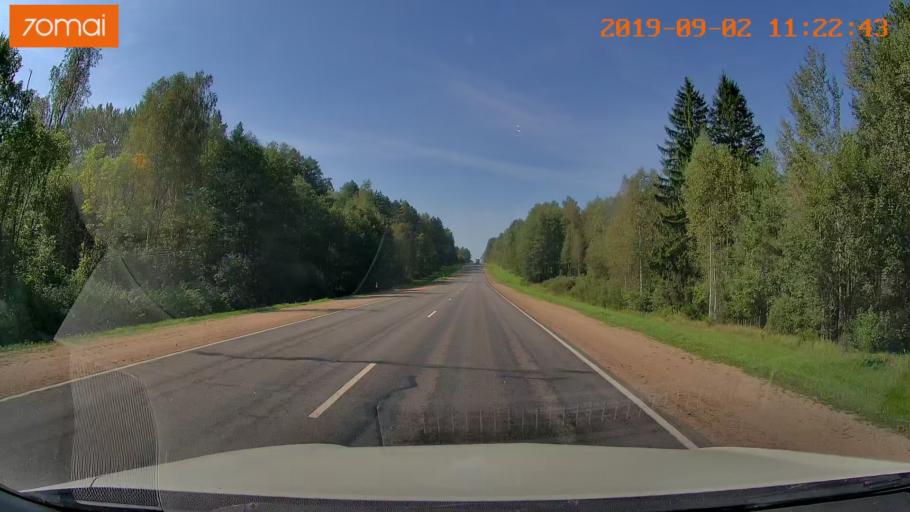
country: RU
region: Smolensk
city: Roslavl'
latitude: 54.0233
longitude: 33.0071
